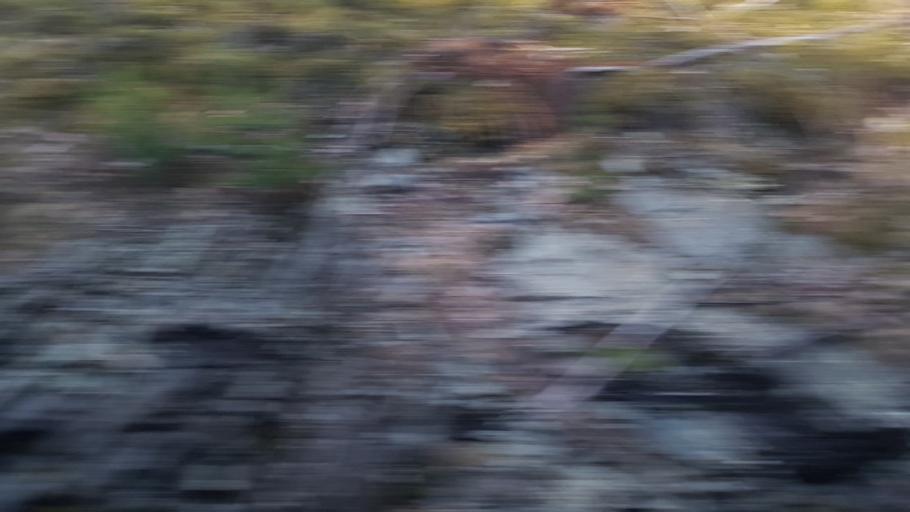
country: NO
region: Sor-Trondelag
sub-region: Trondheim
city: Trondheim
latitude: 63.4300
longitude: 10.5090
